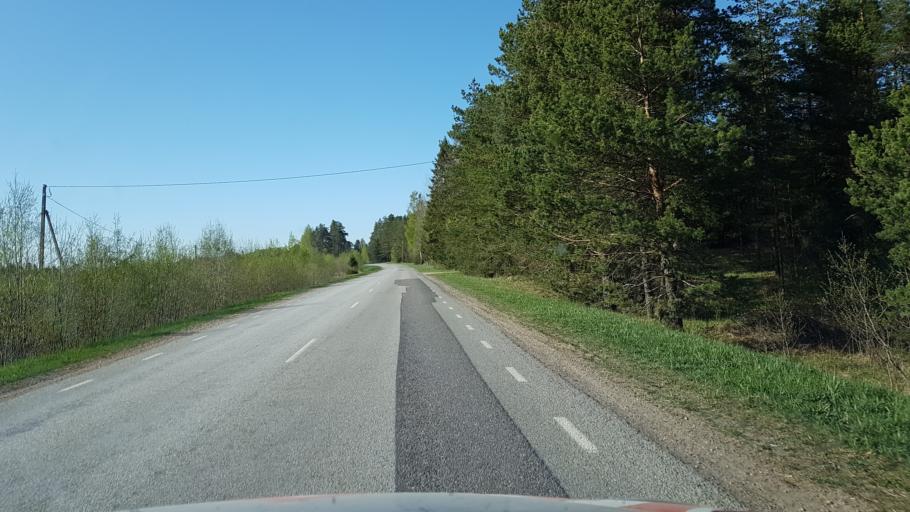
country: EE
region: Paernumaa
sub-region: Paikuse vald
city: Paikuse
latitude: 58.3504
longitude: 24.6666
